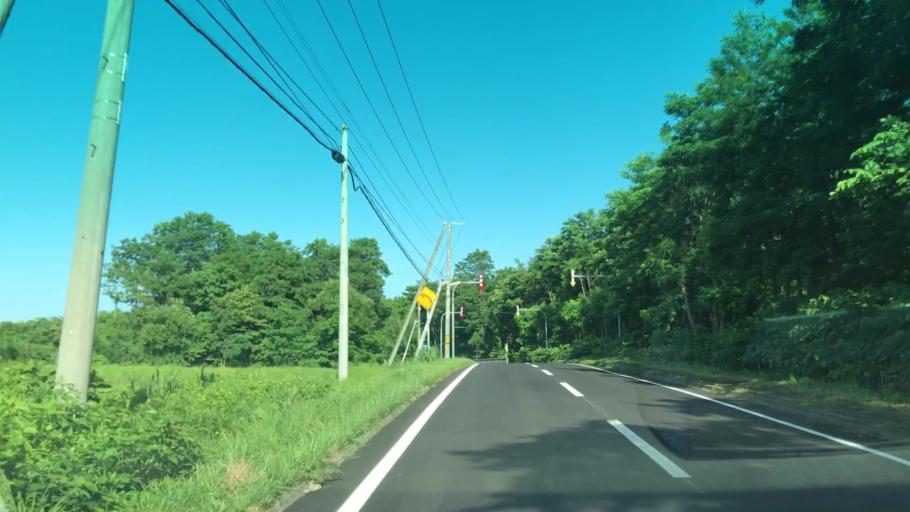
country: JP
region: Hokkaido
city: Yoichi
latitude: 43.0324
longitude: 140.7682
